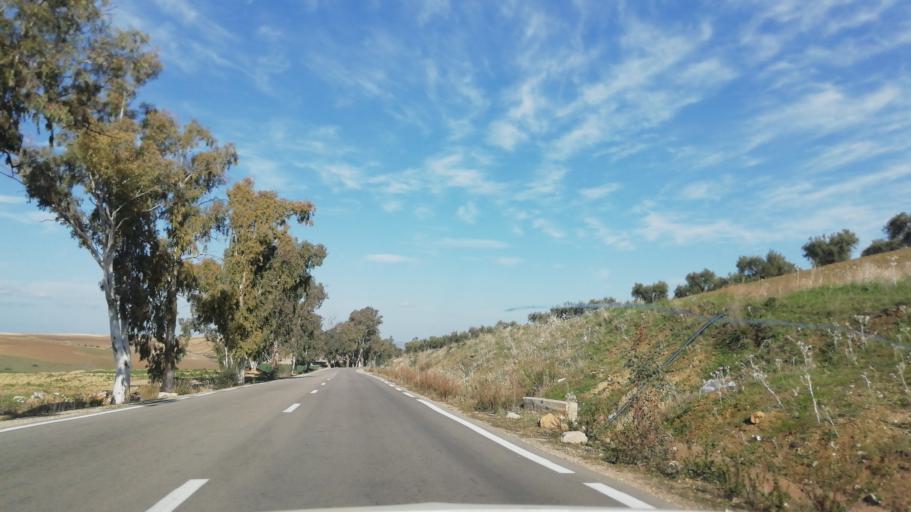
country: DZ
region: Tlemcen
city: Chetouane
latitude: 34.9680
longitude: -1.2461
